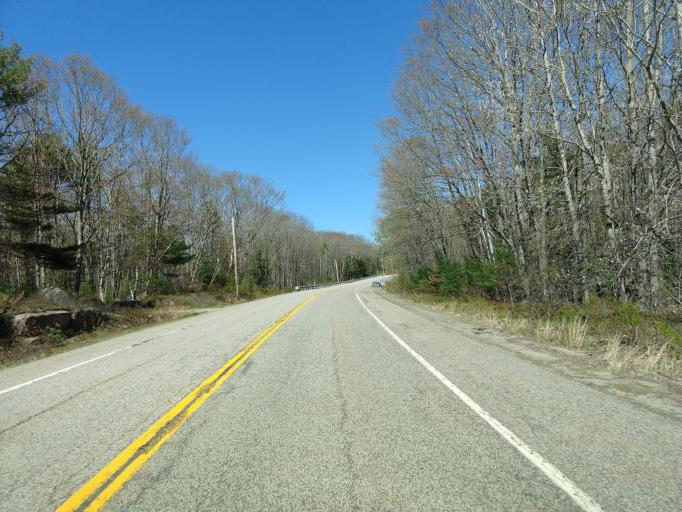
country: US
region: Maine
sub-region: York County
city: Arundel
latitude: 43.4225
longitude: -70.4059
